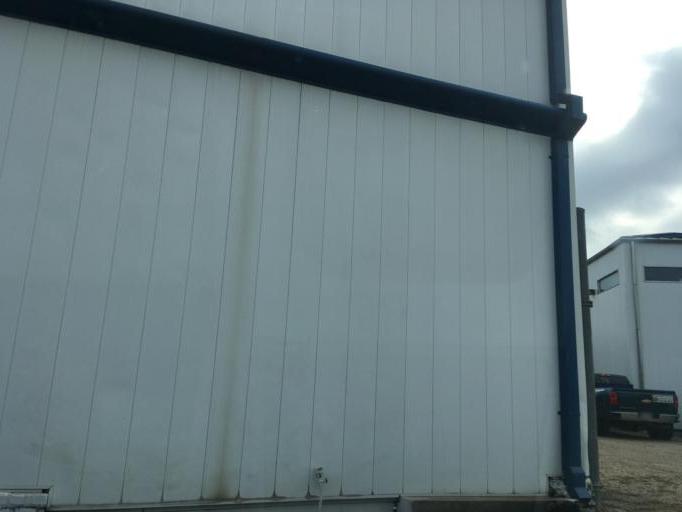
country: US
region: Louisiana
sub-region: Orleans Parish
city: New Orleans
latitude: 29.9863
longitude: -90.0596
